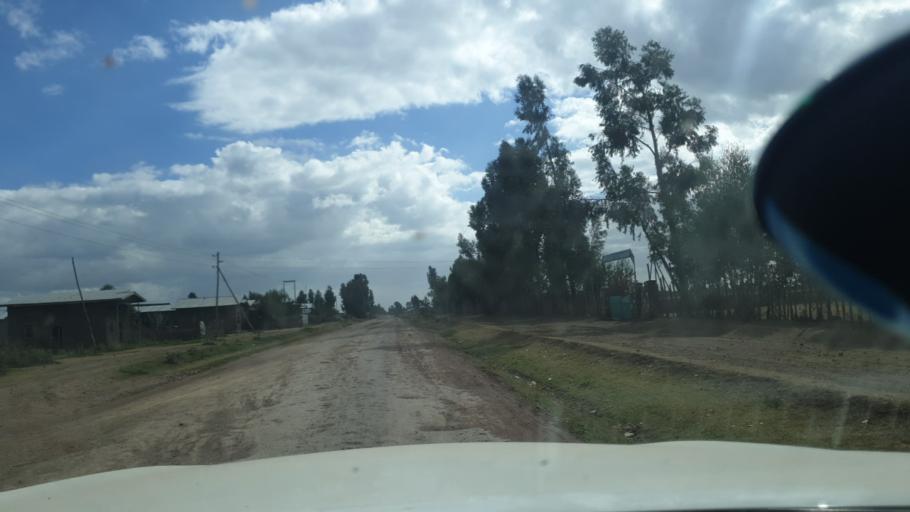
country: ET
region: Oromiya
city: Ziway
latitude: 7.7256
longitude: 39.0291
